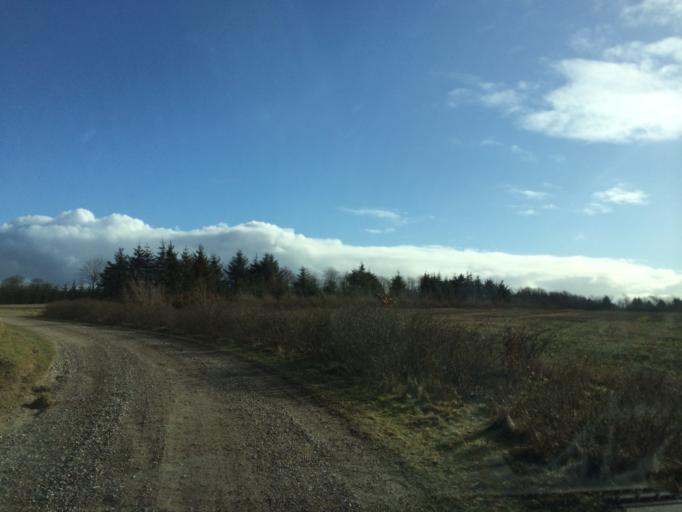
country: DK
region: Central Jutland
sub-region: Holstebro Kommune
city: Ulfborg
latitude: 56.2662
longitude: 8.4128
